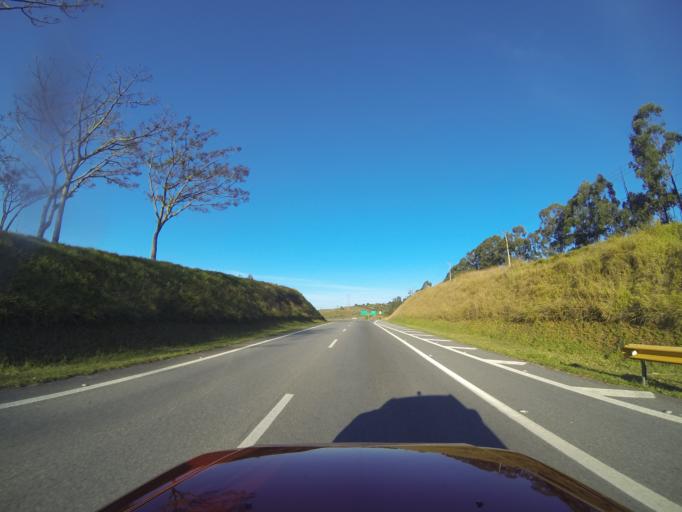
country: BR
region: Sao Paulo
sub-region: Sao Jose Dos Campos
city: Sao Jose dos Campos
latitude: -23.2691
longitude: -45.8233
